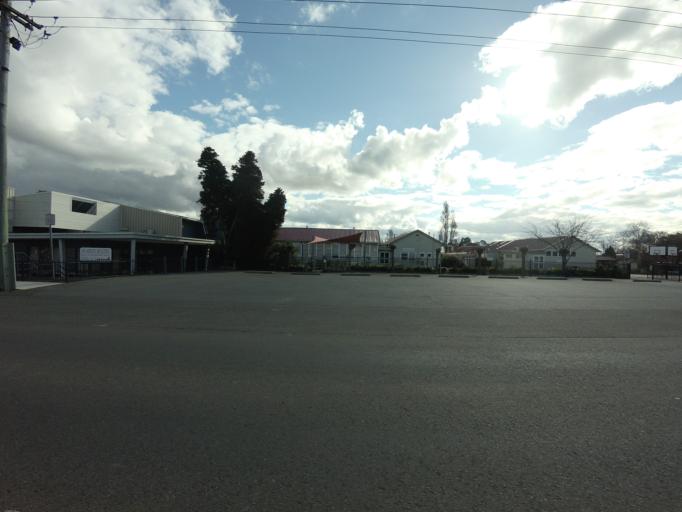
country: AU
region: Tasmania
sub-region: Northern Midlands
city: Longford
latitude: -41.6912
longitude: 147.0792
